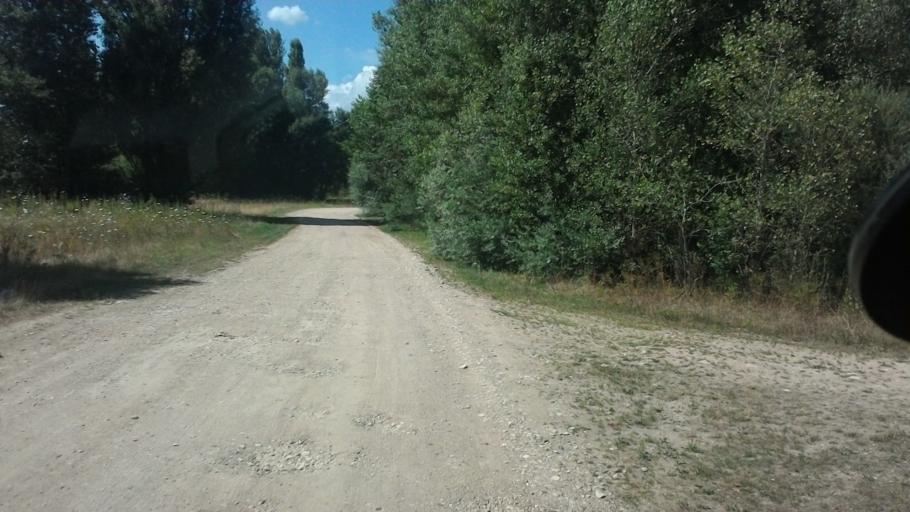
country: FR
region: Bourgogne
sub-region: Departement de la Cote-d'Or
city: Seurre
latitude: 46.9352
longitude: 5.1564
